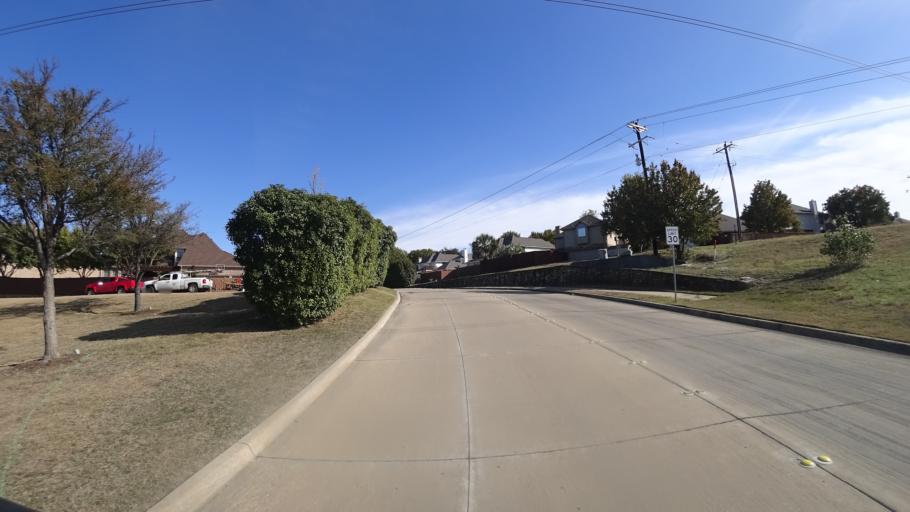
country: US
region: Texas
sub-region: Denton County
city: The Colony
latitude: 33.0273
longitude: -96.9152
